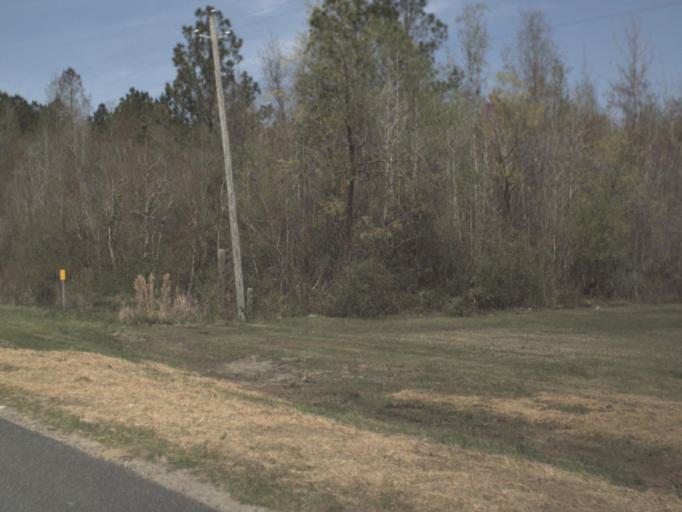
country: US
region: Florida
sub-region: Holmes County
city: Bonifay
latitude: 30.7876
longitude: -85.6643
